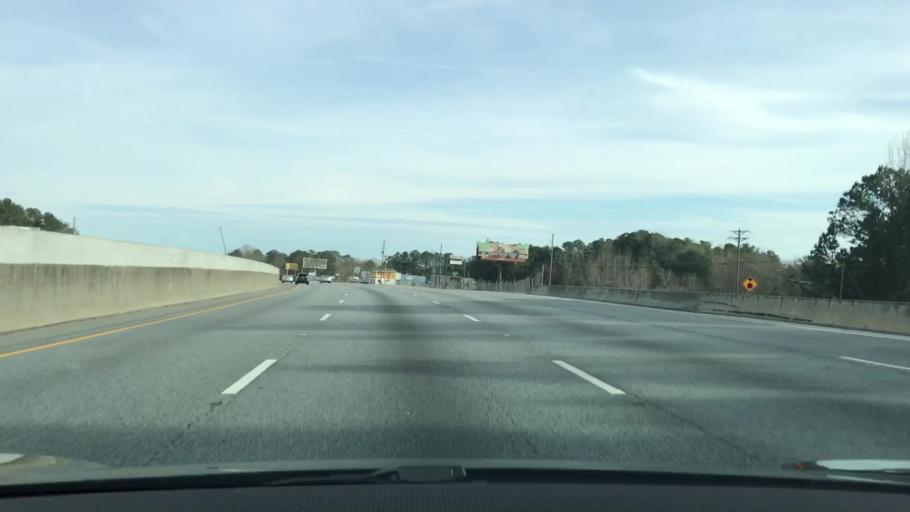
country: US
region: Georgia
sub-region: Rockdale County
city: Conyers
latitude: 33.6326
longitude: -83.9735
